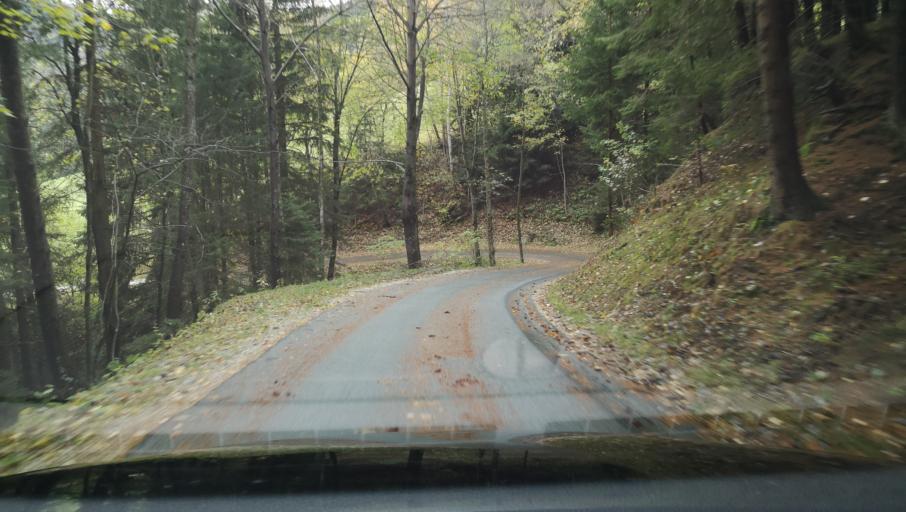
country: AT
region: Styria
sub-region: Politischer Bezirk Weiz
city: Gasen
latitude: 47.3580
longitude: 15.6073
